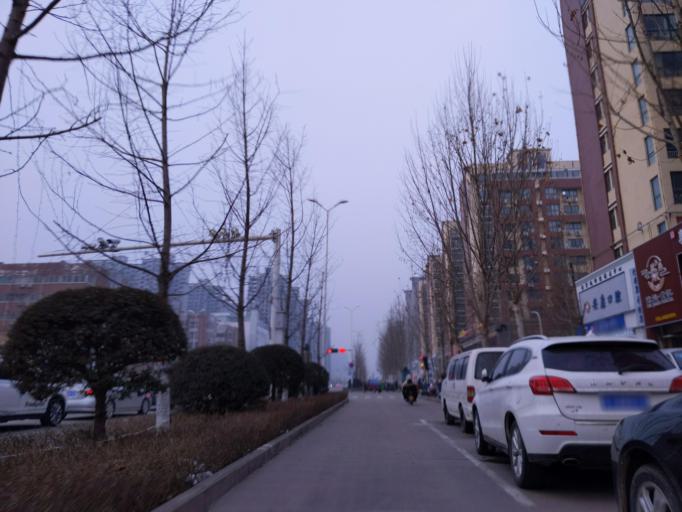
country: CN
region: Henan Sheng
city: Puyang
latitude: 35.7840
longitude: 115.0268
